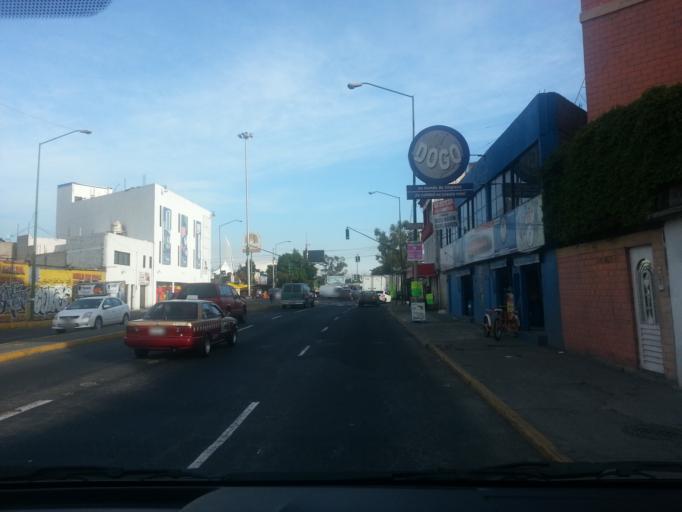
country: MX
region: Mexico City
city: Cuauhtemoc
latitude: 19.4656
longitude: -99.1335
